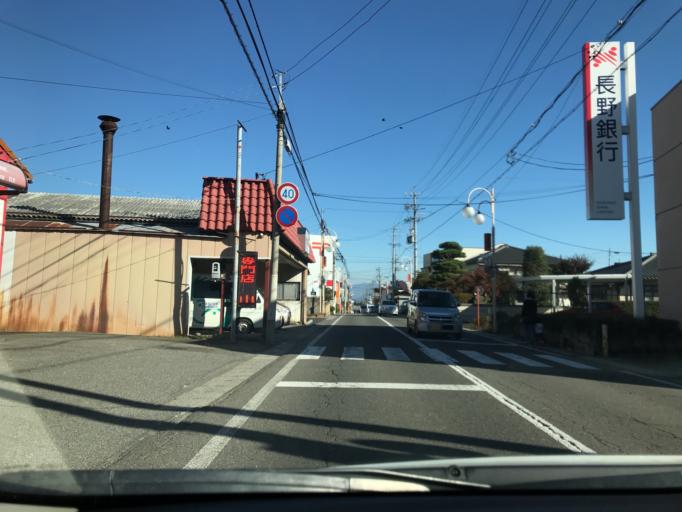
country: JP
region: Nagano
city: Toyoshina
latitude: 36.1952
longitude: 137.8543
